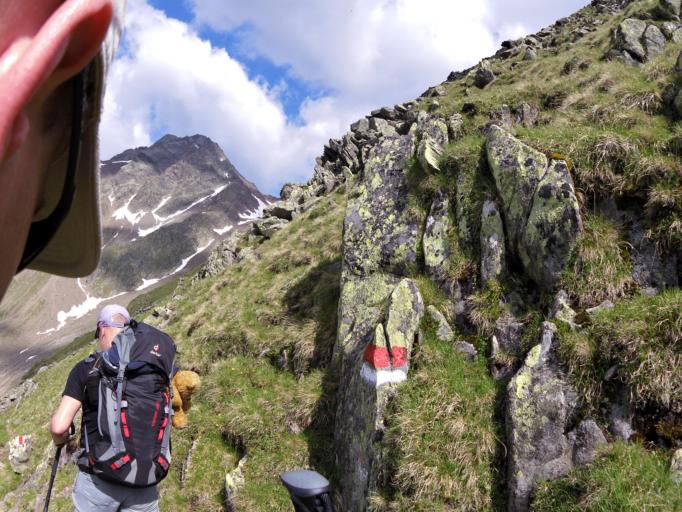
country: AT
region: Tyrol
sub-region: Politischer Bezirk Innsbruck Land
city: Gschnitz
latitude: 47.0323
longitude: 11.3001
